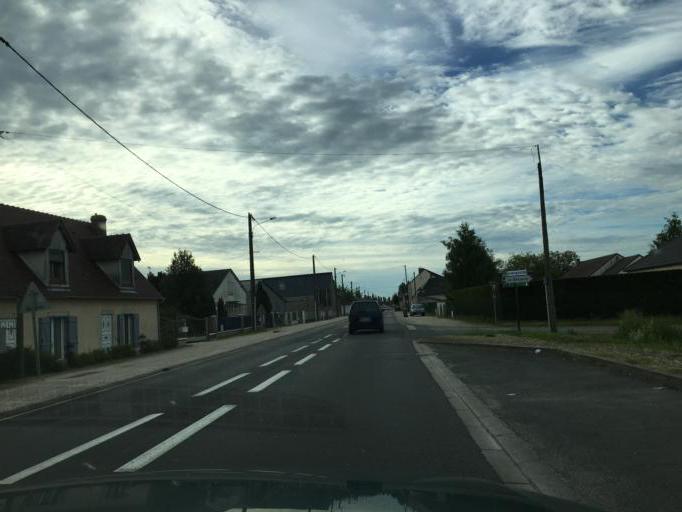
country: FR
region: Centre
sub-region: Departement du Loiret
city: Bricy
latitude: 47.9690
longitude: 1.7776
